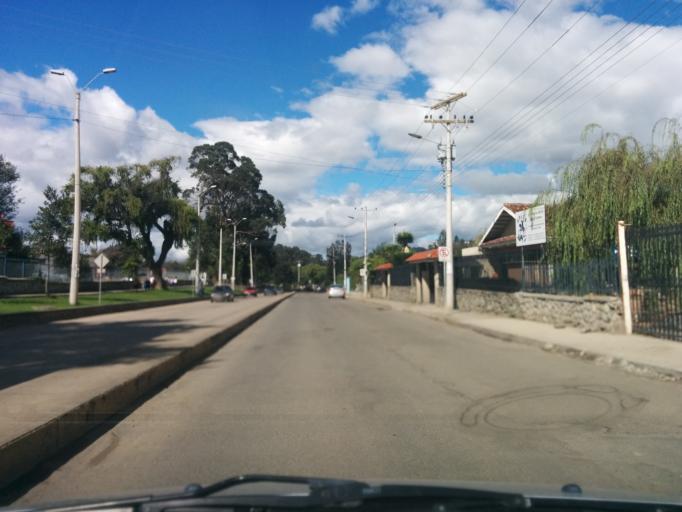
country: EC
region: Azuay
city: Cuenca
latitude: -2.9123
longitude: -78.9925
